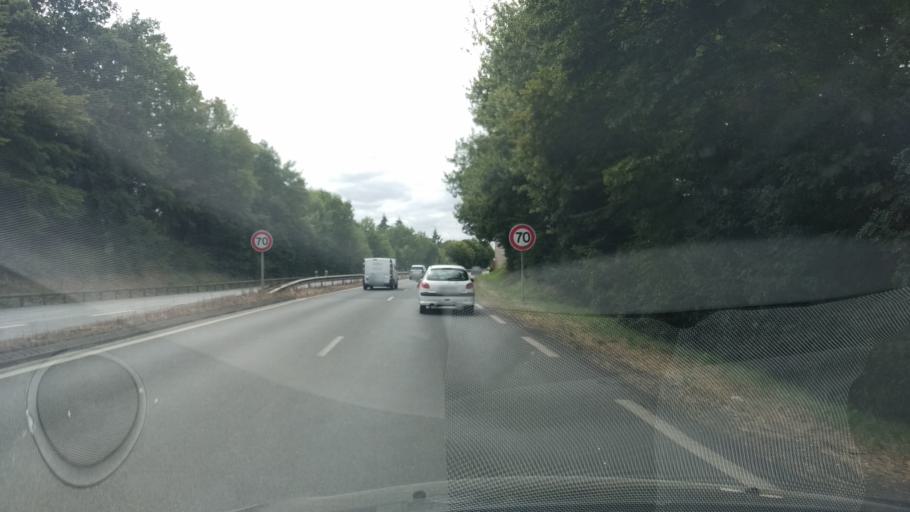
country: FR
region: Poitou-Charentes
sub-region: Departement de la Vienne
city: Saint-Benoit
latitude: 46.5518
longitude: 0.3201
